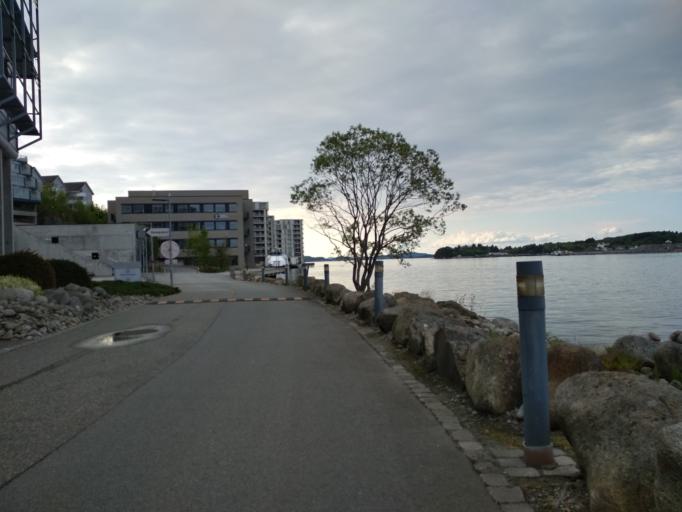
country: NO
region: Rogaland
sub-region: Stavanger
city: Stavanger
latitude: 58.9794
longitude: 5.7203
